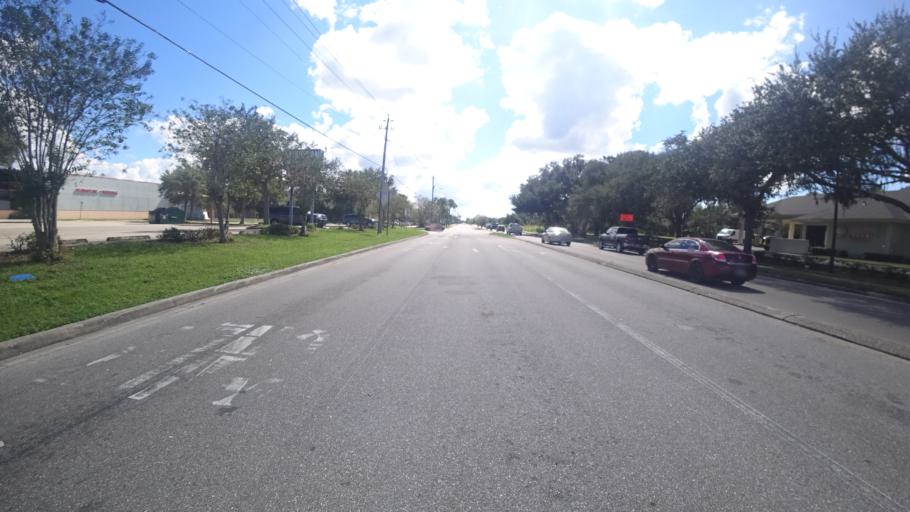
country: US
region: Florida
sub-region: Manatee County
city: Memphis
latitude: 27.5210
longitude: -82.5525
